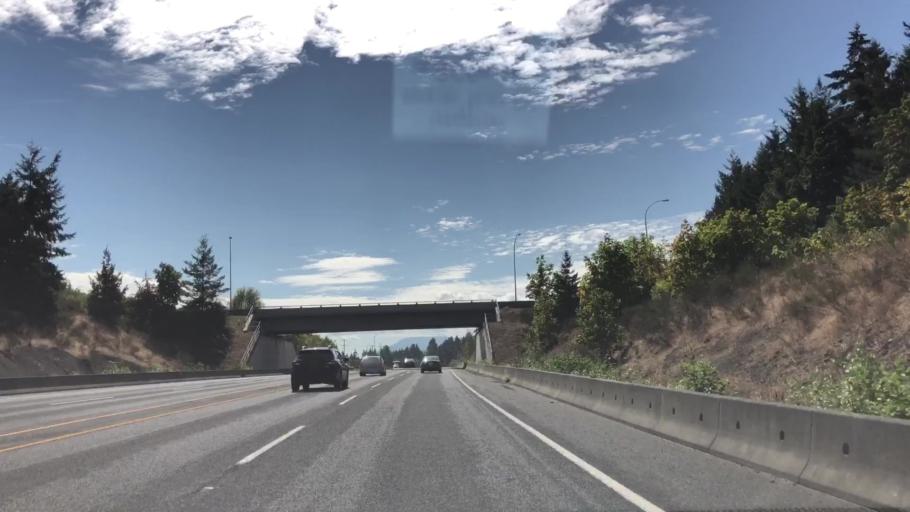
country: CA
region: British Columbia
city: Nanaimo
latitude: 49.1266
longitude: -123.8638
